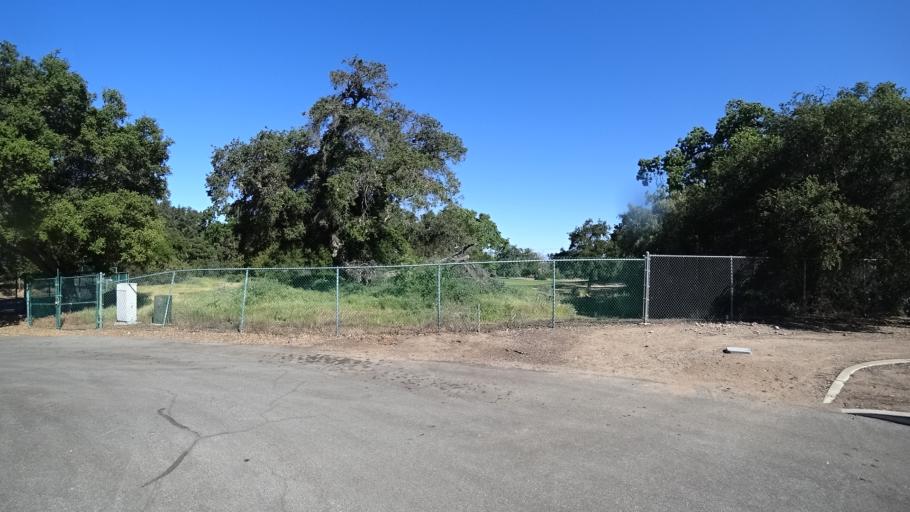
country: US
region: California
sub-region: Ventura County
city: Thousand Oaks
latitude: 34.1762
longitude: -118.8866
